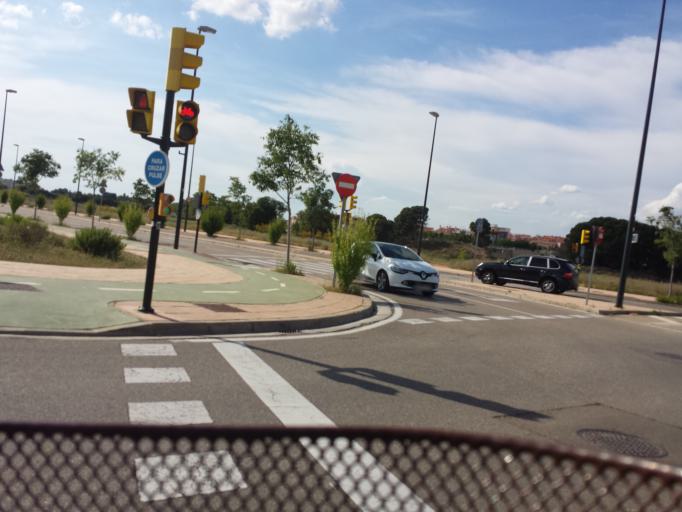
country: ES
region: Aragon
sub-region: Provincia de Zaragoza
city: Montecanal
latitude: 41.6324
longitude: -0.9307
